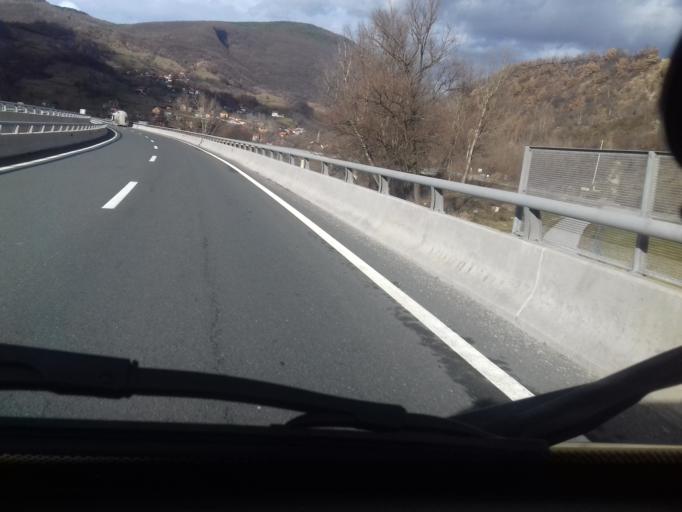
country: BA
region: Federation of Bosnia and Herzegovina
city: Kakanj
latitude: 44.1339
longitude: 18.0833
